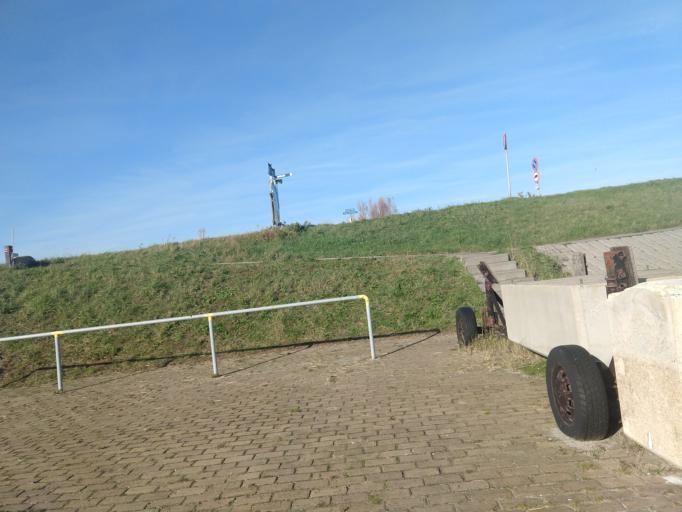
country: NL
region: Zeeland
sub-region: Schouwen-Duiveland
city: Haamstede
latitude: 51.6753
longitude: 3.7543
